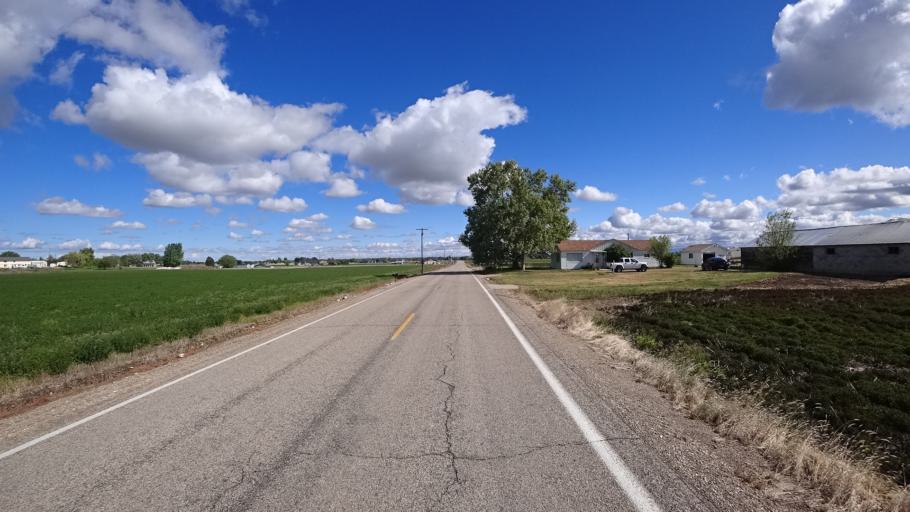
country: US
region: Idaho
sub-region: Ada County
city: Kuna
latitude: 43.5148
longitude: -116.4736
